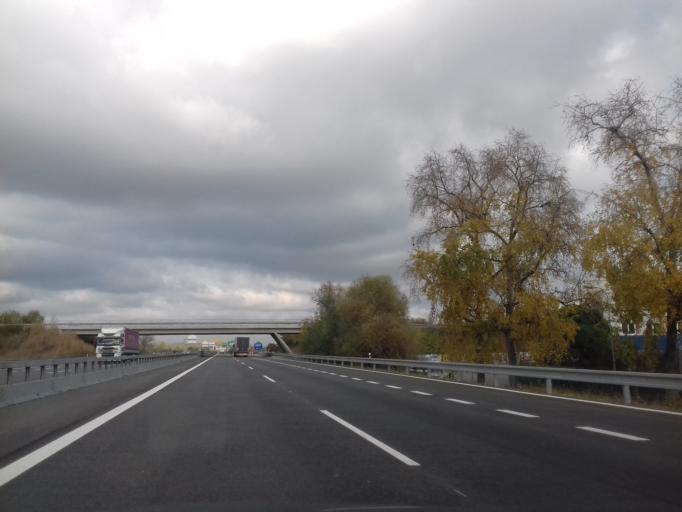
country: CZ
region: South Moravian
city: Modrice
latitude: 49.1338
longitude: 16.6383
